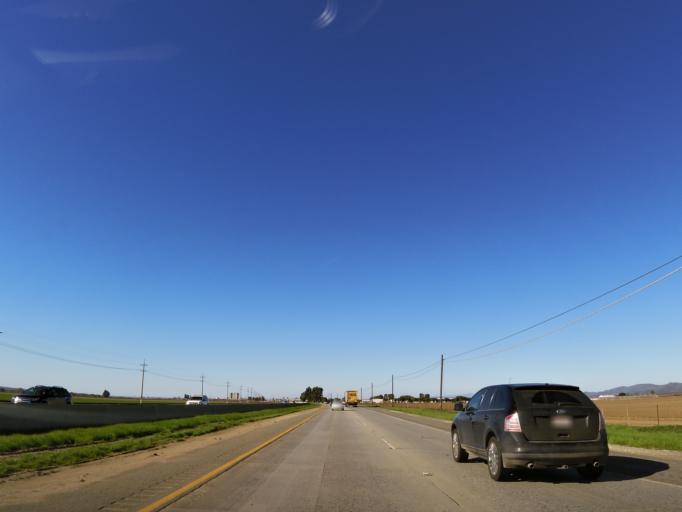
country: US
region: California
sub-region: Monterey County
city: Chualar
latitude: 36.5993
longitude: -121.5492
